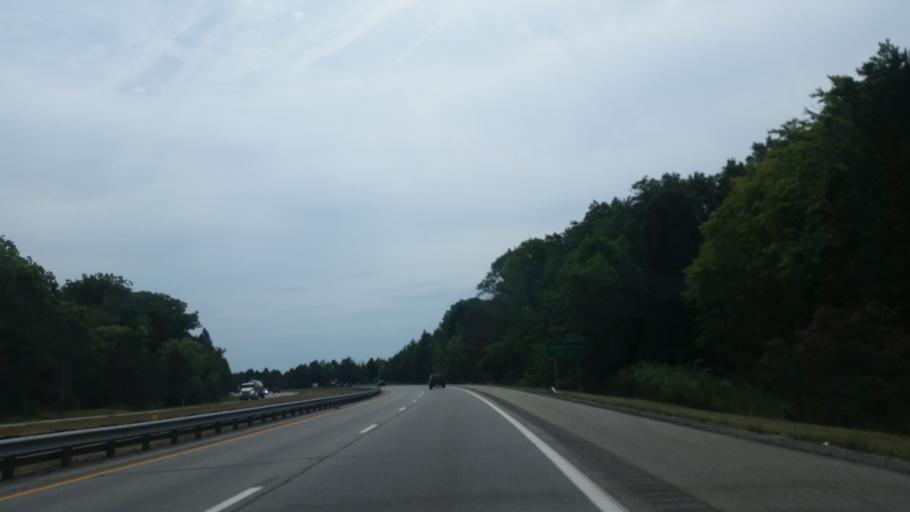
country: US
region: Ohio
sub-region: Cuyahoga County
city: Solon
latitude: 41.3960
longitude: -81.4497
